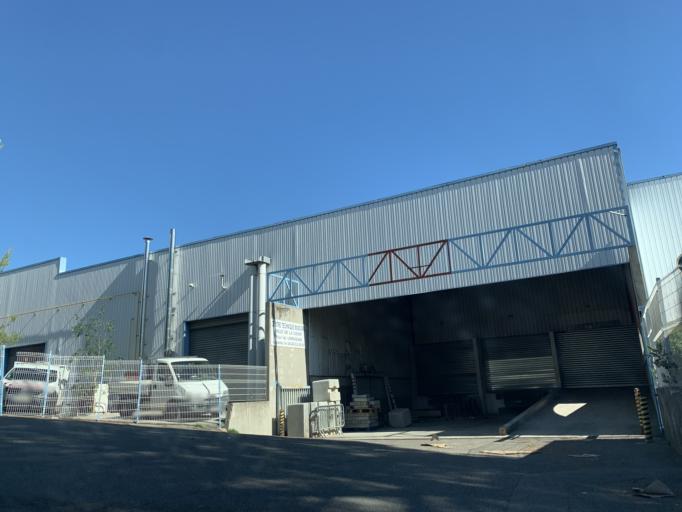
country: FR
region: Provence-Alpes-Cote d'Azur
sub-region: Departement des Bouches-du-Rhone
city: La Ciotat
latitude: 43.2009
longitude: 5.5974
